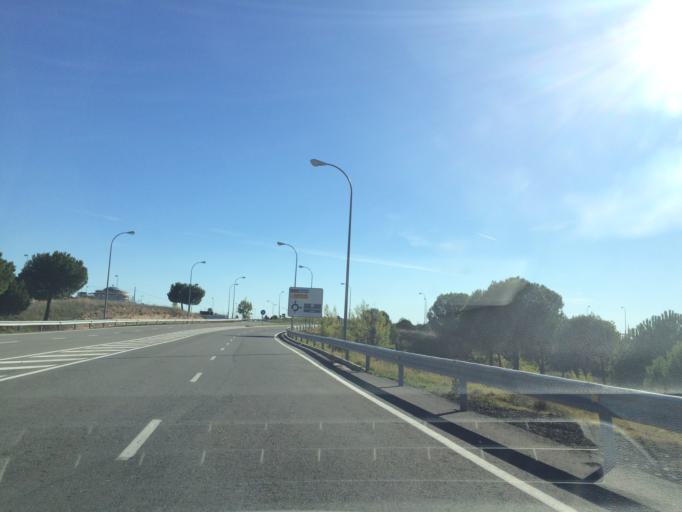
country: ES
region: Madrid
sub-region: Provincia de Madrid
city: Tres Cantos
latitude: 40.6041
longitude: -3.7215
